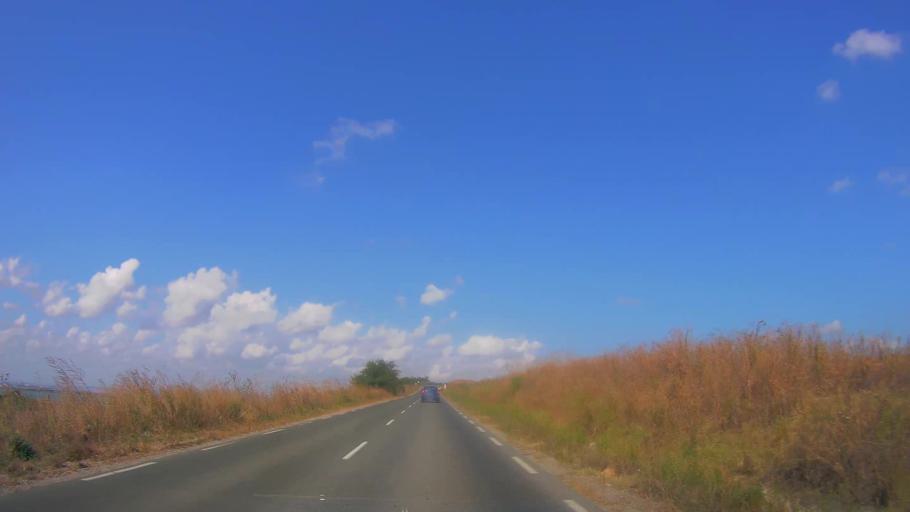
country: BG
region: Burgas
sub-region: Obshtina Burgas
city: Burgas
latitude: 42.4781
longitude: 27.3717
